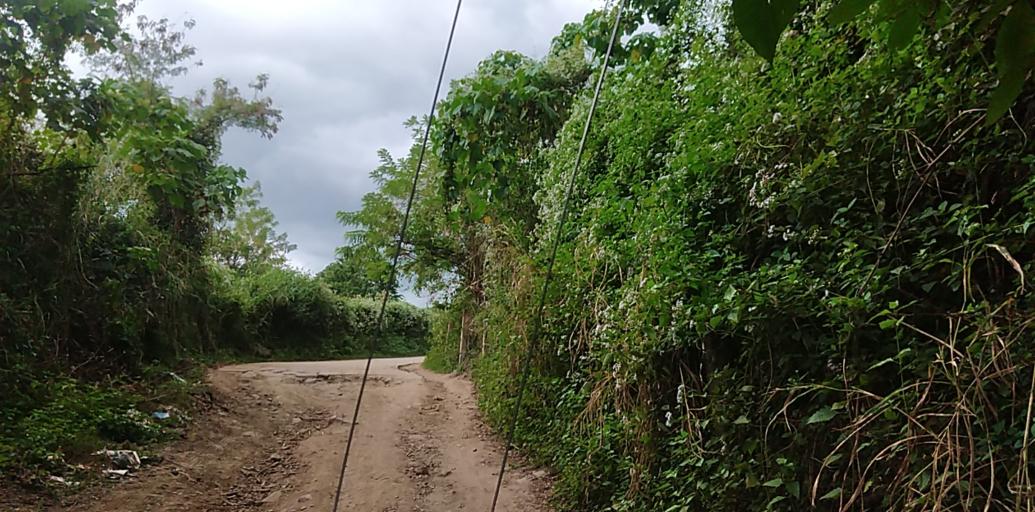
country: PH
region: Central Luzon
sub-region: Province of Pampanga
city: Babo-Pangulo
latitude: 15.1109
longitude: 120.4961
